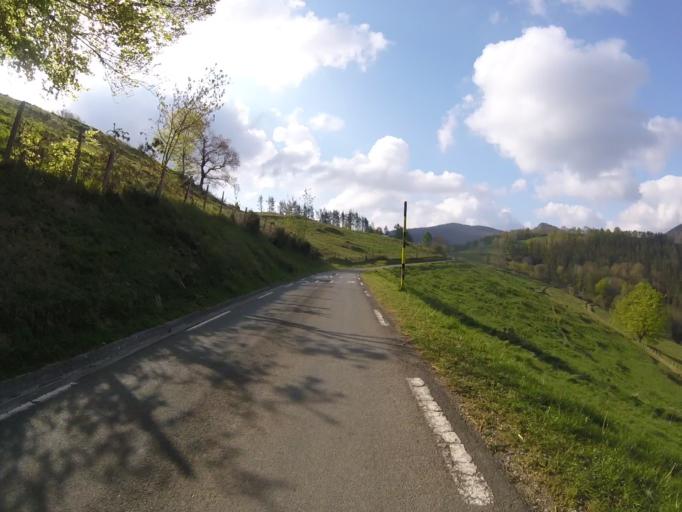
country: ES
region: Basque Country
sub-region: Provincia de Guipuzcoa
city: Azkoitia
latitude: 43.2218
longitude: -2.3103
